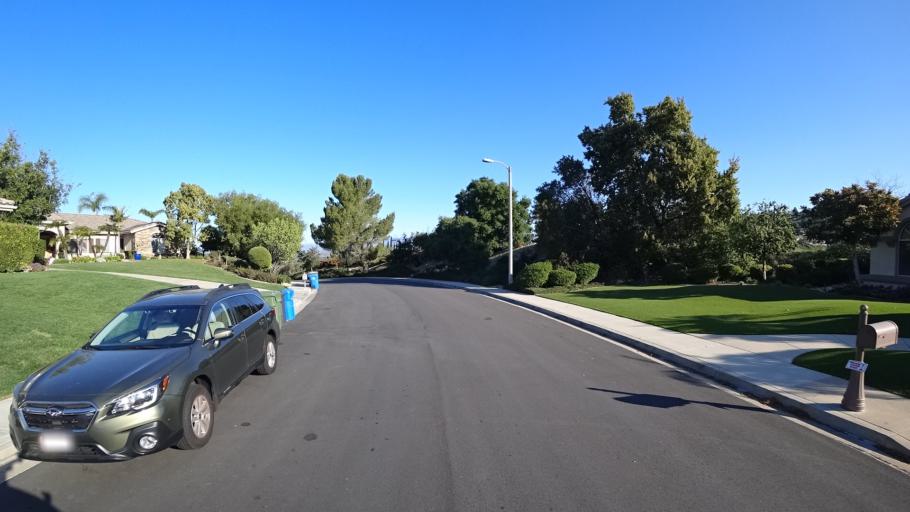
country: US
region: California
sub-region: Ventura County
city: Thousand Oaks
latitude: 34.1869
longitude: -118.8390
